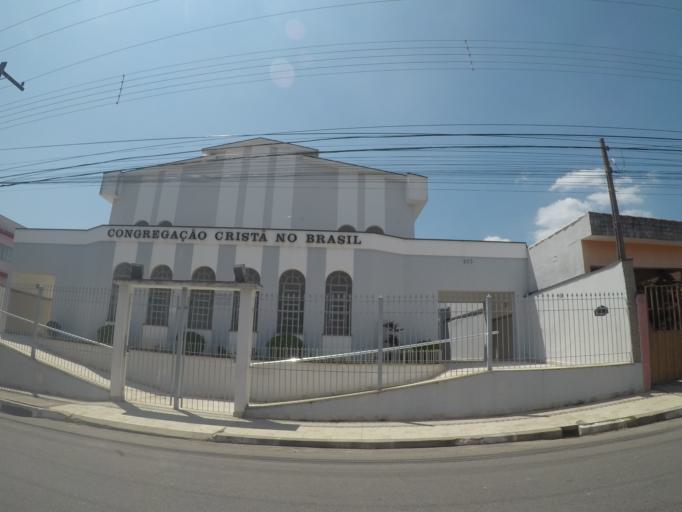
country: BR
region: Sao Paulo
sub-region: Cabreuva
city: Cabreuva
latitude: -23.2496
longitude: -47.0562
